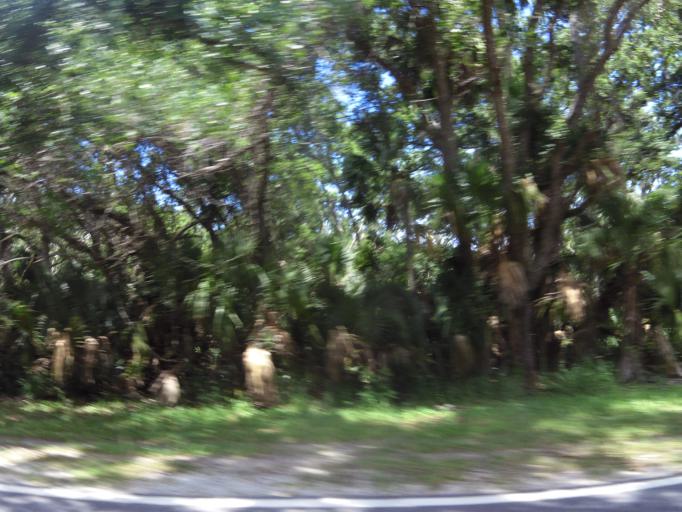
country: US
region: Florida
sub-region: Volusia County
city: Ormond-by-the-Sea
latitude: 29.3665
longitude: -81.1251
